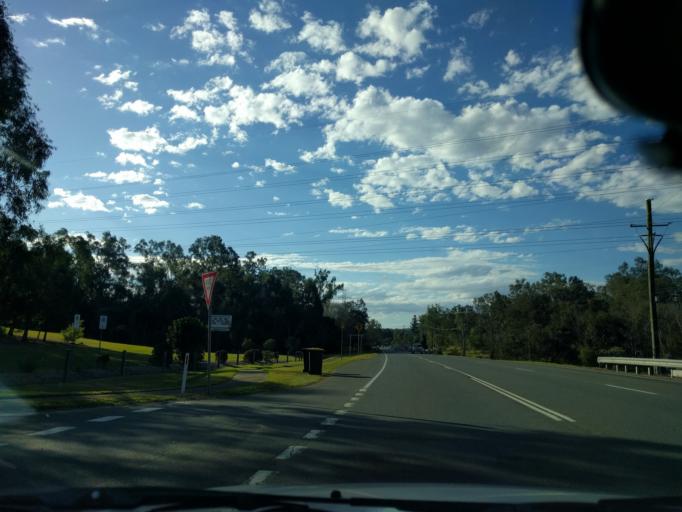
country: AU
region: Queensland
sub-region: Brisbane
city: Riverhills
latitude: -27.5508
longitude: 152.8891
